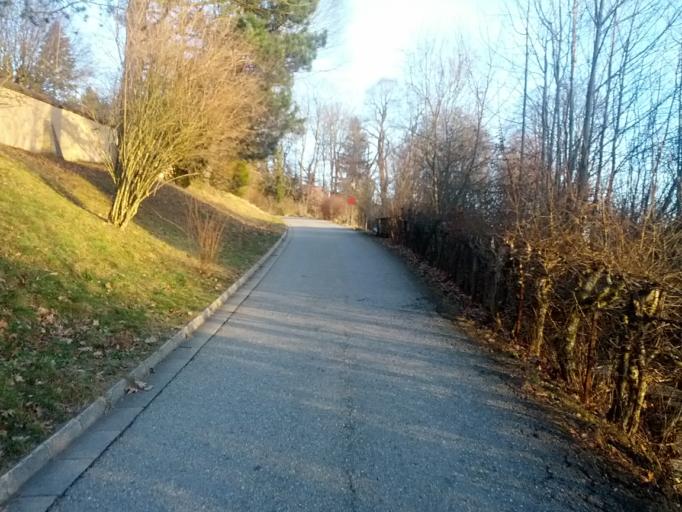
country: DE
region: Bavaria
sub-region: Swabia
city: Kronburg
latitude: 47.9034
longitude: 10.1590
